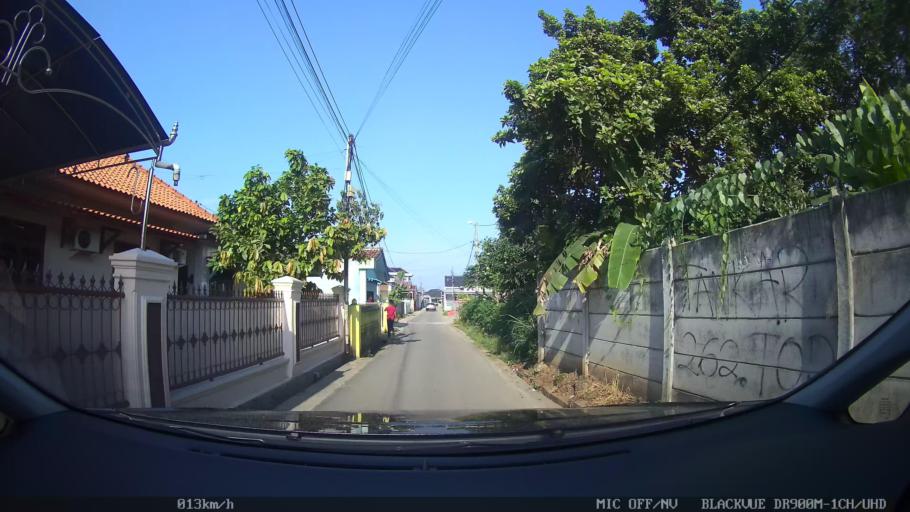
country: ID
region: Lampung
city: Kedaton
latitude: -5.3699
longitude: 105.2293
